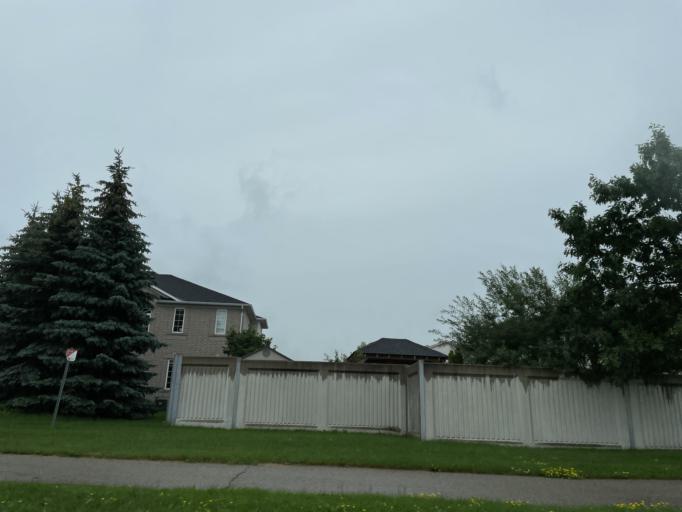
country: CA
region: Ontario
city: Cambridge
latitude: 43.4083
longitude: -80.2827
